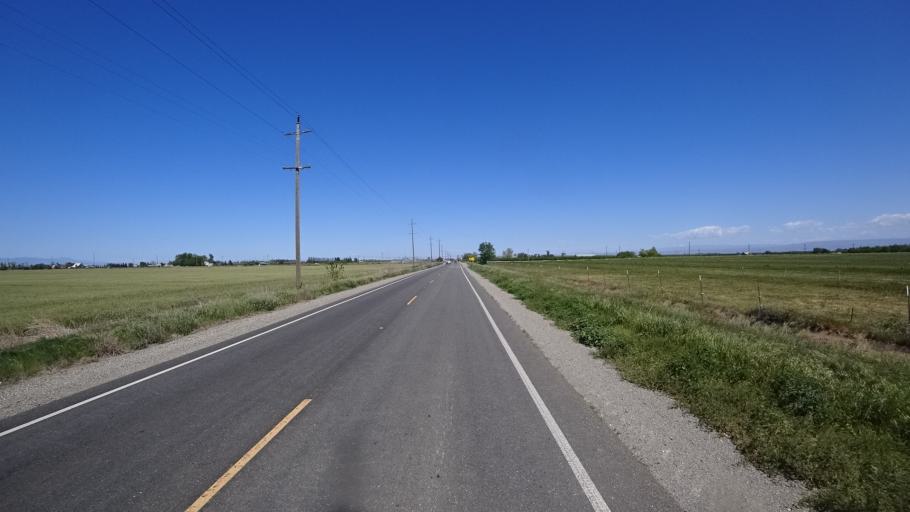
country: US
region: California
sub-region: Glenn County
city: Orland
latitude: 39.7657
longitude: -122.1409
